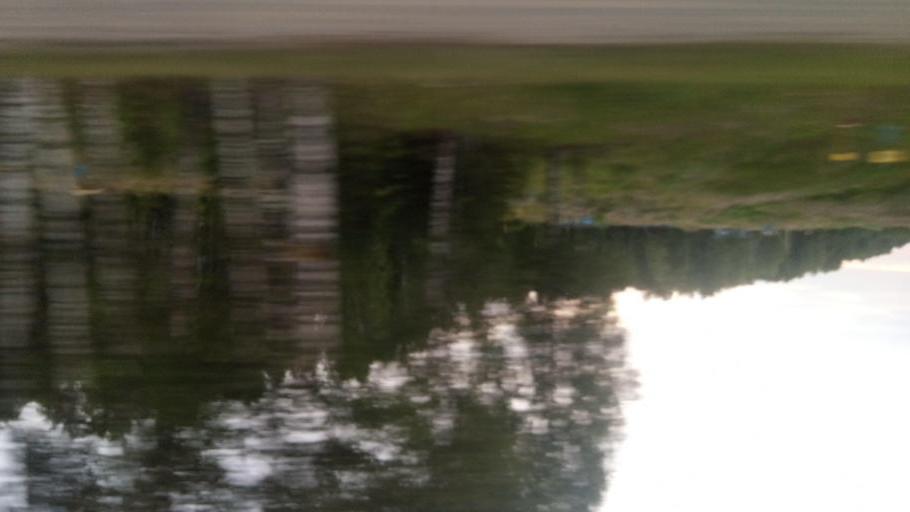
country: RU
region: Chelyabinsk
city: Sargazy
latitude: 54.9713
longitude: 61.2201
